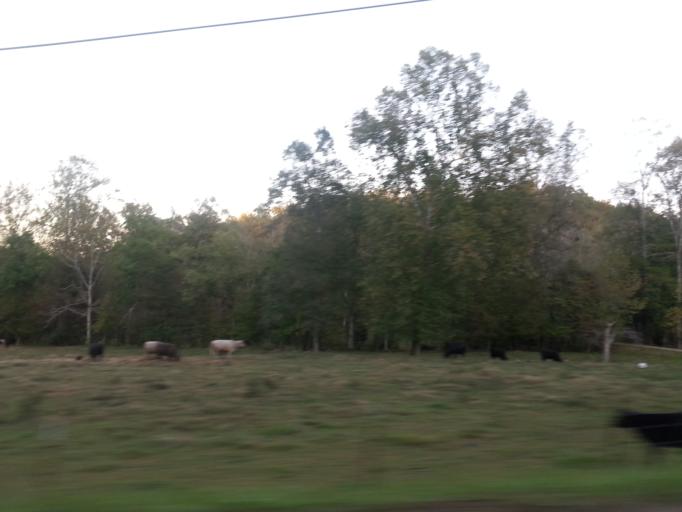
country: US
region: Tennessee
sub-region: Blount County
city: Wildwood
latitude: 35.7833
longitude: -83.7686
